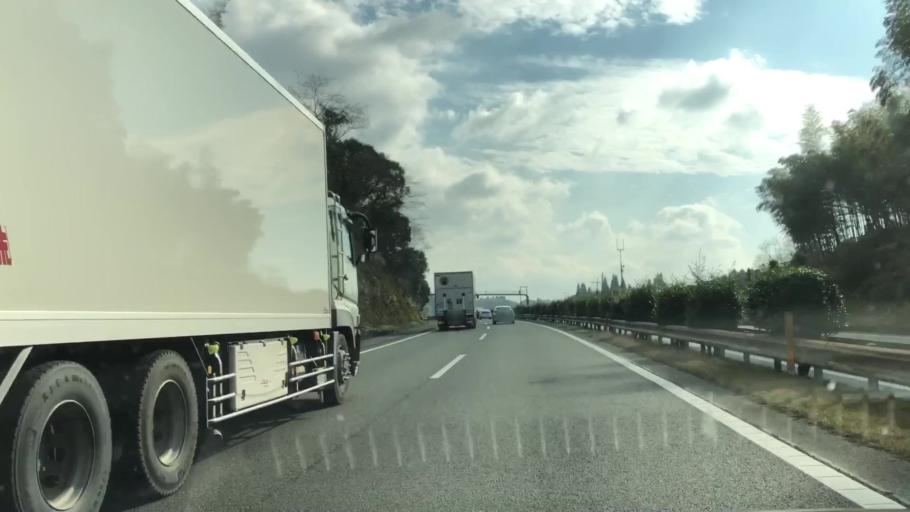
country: JP
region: Fukuoka
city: Setakamachi-takayanagi
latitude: 33.0897
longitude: 130.5392
